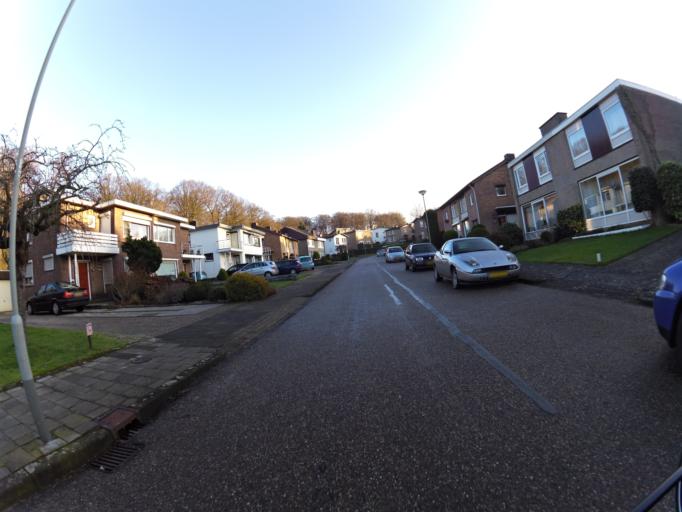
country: NL
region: Limburg
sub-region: Gemeente Heerlen
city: Heerlen
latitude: 50.9024
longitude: 6.0115
